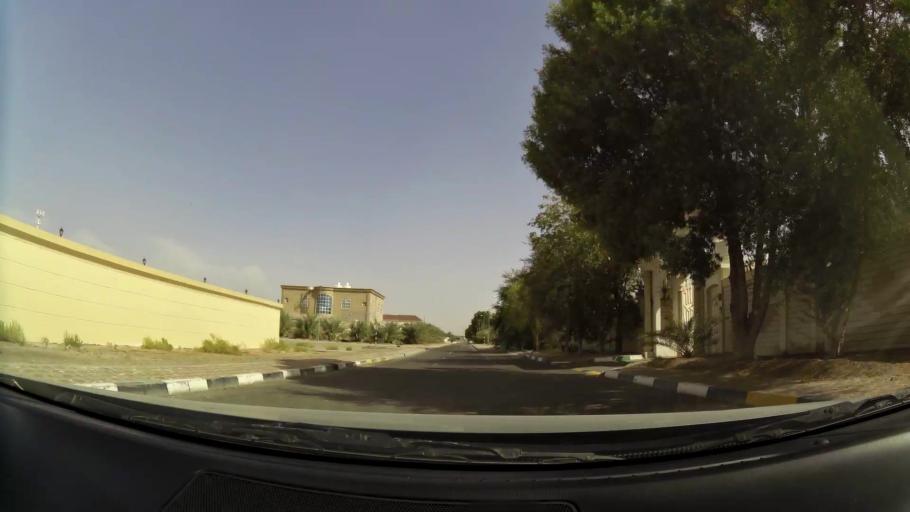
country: AE
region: Abu Dhabi
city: Al Ain
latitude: 24.2450
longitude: 55.6896
